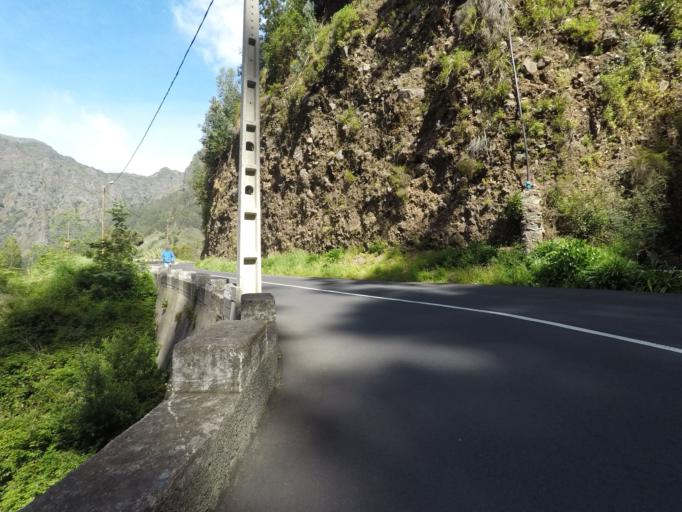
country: PT
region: Madeira
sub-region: Camara de Lobos
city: Curral das Freiras
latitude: 32.7179
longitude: -16.9628
